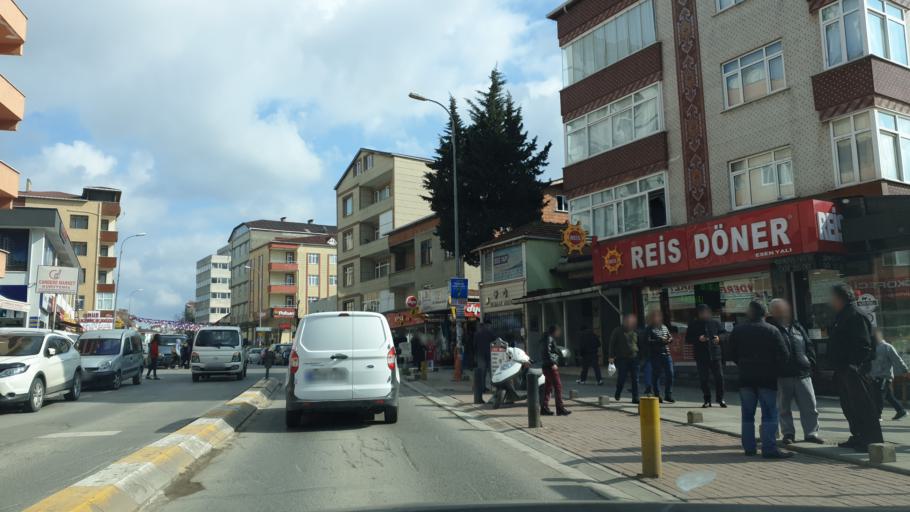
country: TR
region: Istanbul
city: Icmeler
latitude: 40.8677
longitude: 29.2976
